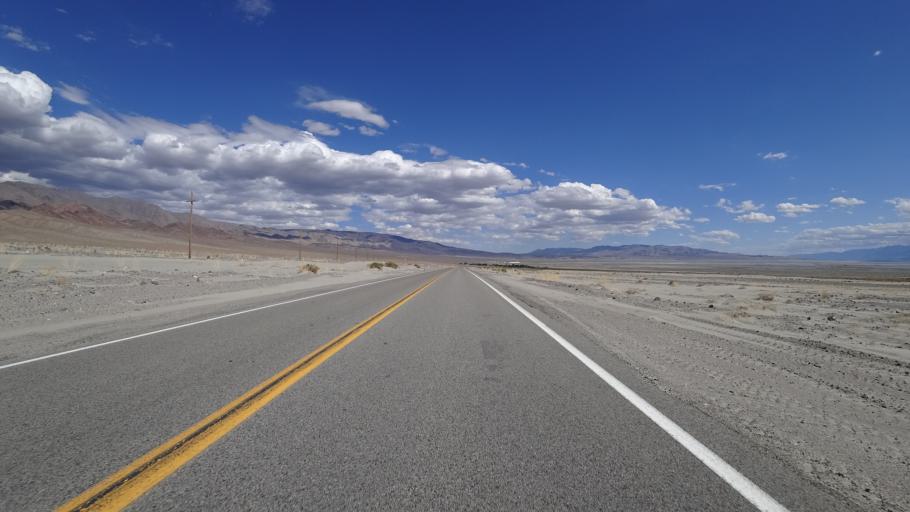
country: US
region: California
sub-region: Inyo County
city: Lone Pine
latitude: 36.5051
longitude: -117.8877
